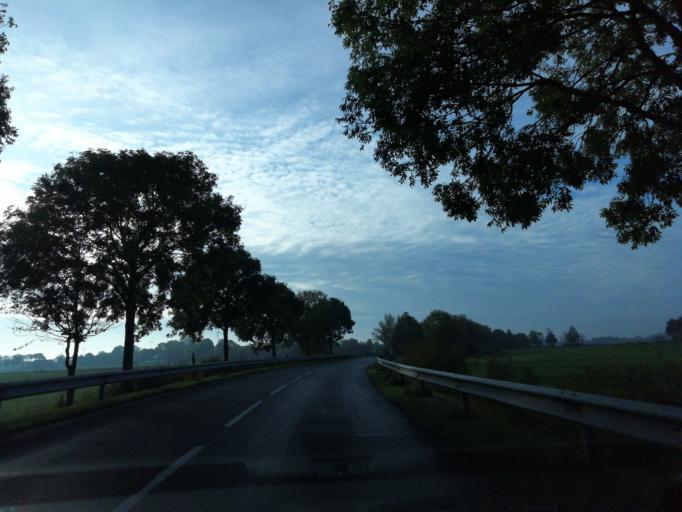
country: DE
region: Lower Saxony
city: Sillenstede
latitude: 53.6303
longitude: 8.0153
